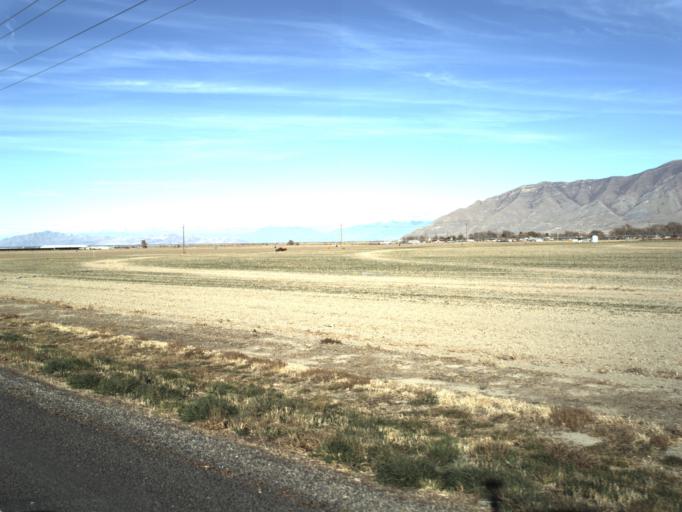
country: US
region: Utah
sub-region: Tooele County
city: Erda
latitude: 40.5981
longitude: -112.3705
